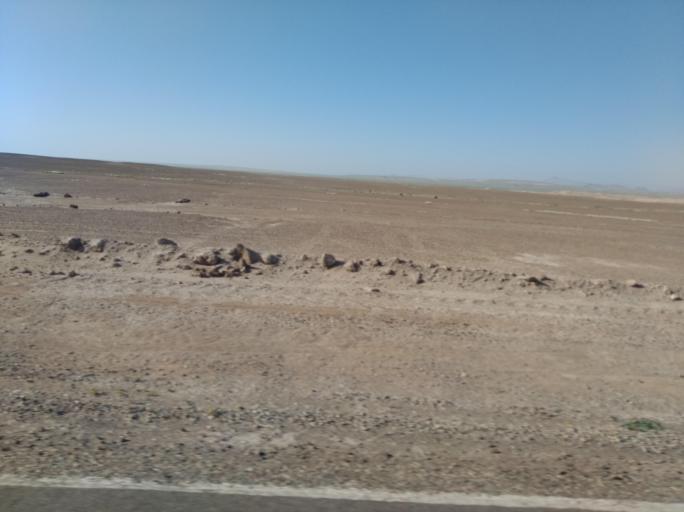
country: CL
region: Atacama
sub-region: Provincia de Copiapo
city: Copiapo
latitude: -27.3166
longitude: -70.8363
